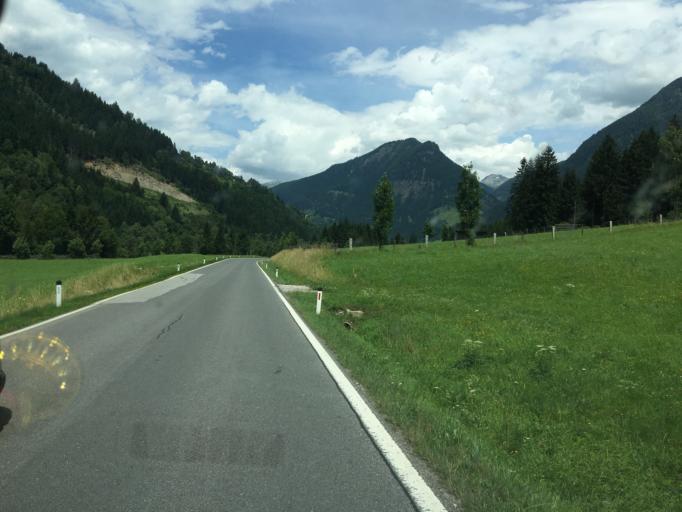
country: AT
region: Carinthia
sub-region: Politischer Bezirk Spittal an der Drau
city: Mortschach
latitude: 46.8951
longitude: 12.9017
